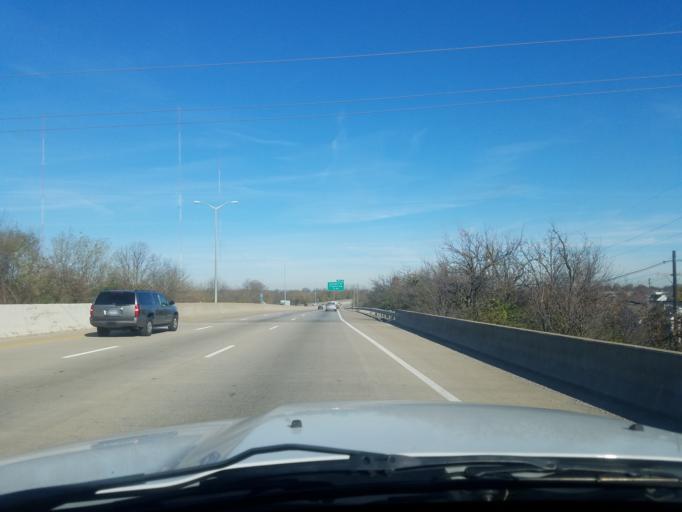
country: US
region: Kentucky
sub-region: Jefferson County
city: Shively
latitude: 38.2276
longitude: -85.8215
